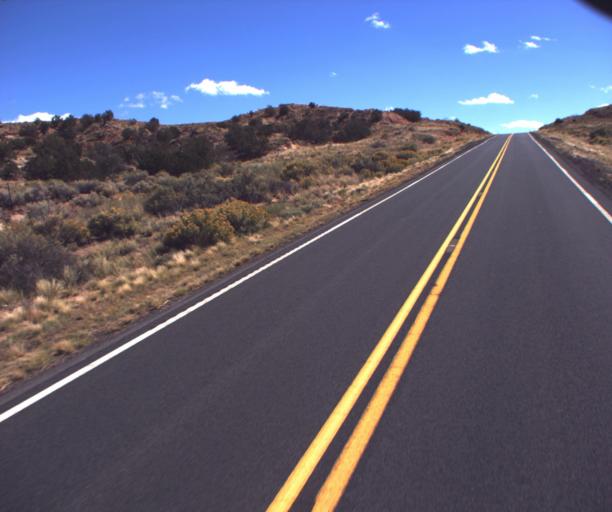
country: US
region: Arizona
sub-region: Apache County
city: Houck
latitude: 35.0352
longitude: -109.2631
